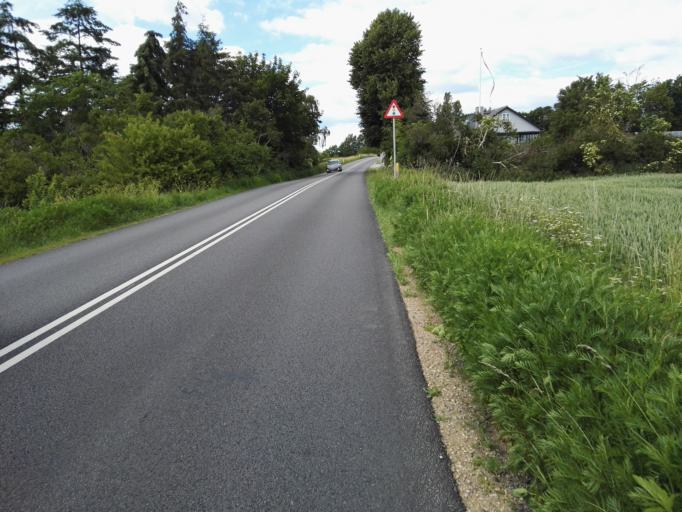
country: DK
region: Capital Region
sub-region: Egedal Kommune
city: Olstykke
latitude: 55.7679
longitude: 12.1481
